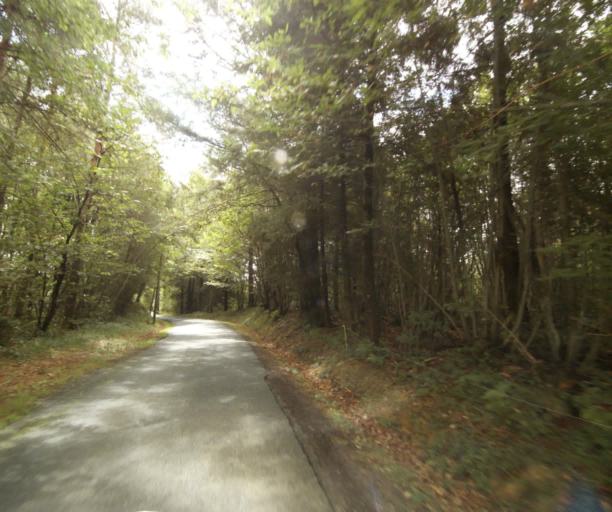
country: FR
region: Limousin
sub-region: Departement de la Correze
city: Sainte-Fortunade
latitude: 45.1674
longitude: 1.8033
